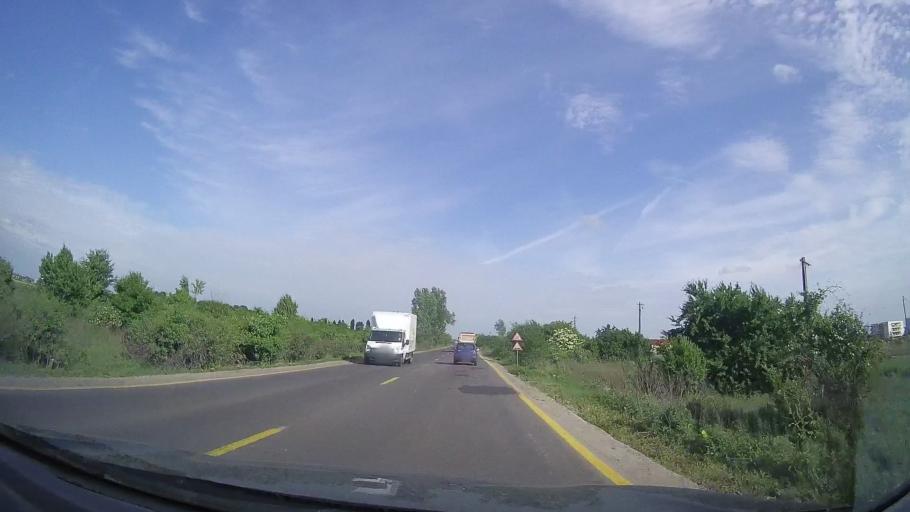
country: RO
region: Ilfov
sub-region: Comuna Magurele
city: Varteju
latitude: 44.3727
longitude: 26.0087
